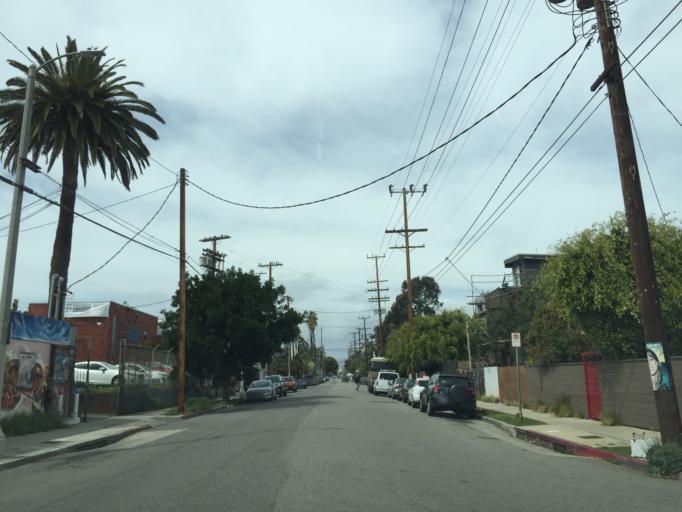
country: US
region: California
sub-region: Los Angeles County
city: Marina del Rey
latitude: 33.9936
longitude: -118.4741
